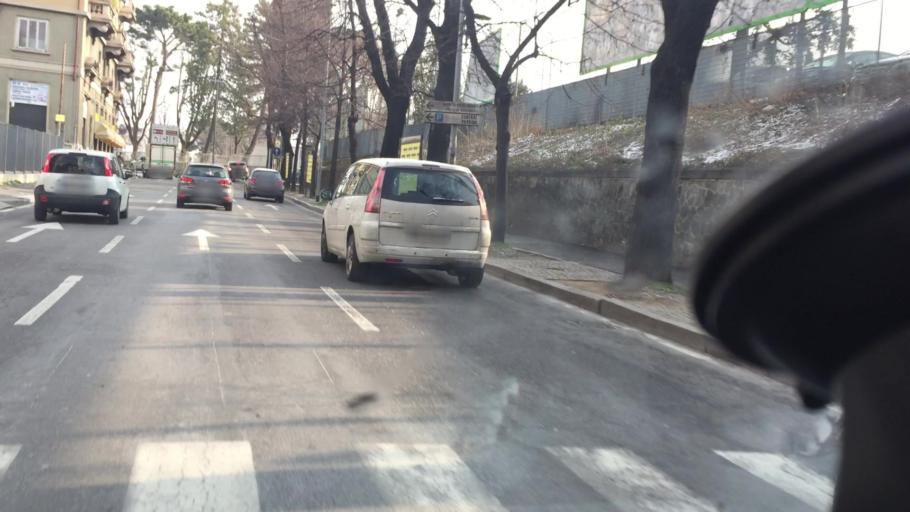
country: IT
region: Lombardy
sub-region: Provincia di Bergamo
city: Bergamo
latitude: 45.6901
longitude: 9.6728
